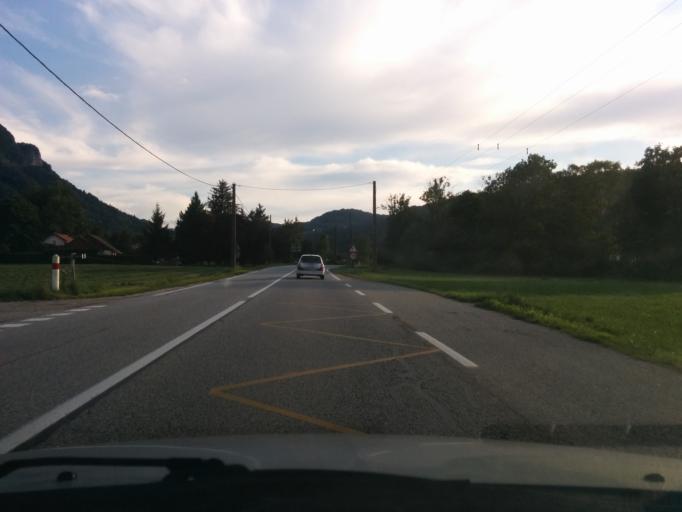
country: FR
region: Rhone-Alpes
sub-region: Departement de l'Isere
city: Saint-Joseph-de-Riviere
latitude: 45.3642
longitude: 5.6825
